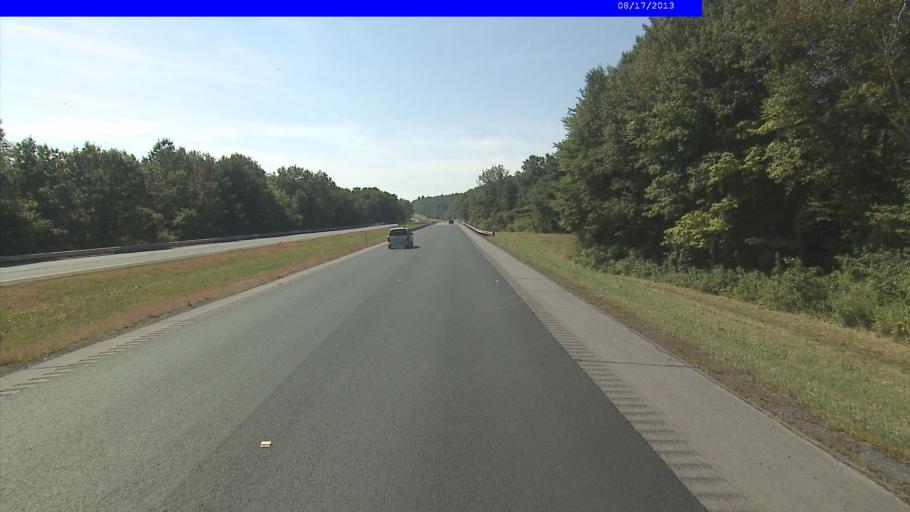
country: US
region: Vermont
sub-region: Windham County
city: Bellows Falls
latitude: 43.0524
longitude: -72.4705
